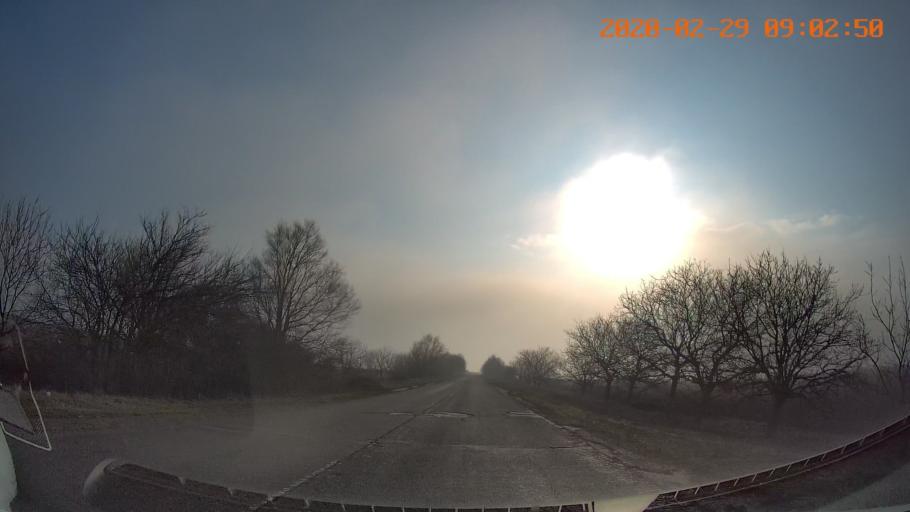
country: UA
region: Odessa
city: Velykoploske
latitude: 46.9190
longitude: 29.7177
